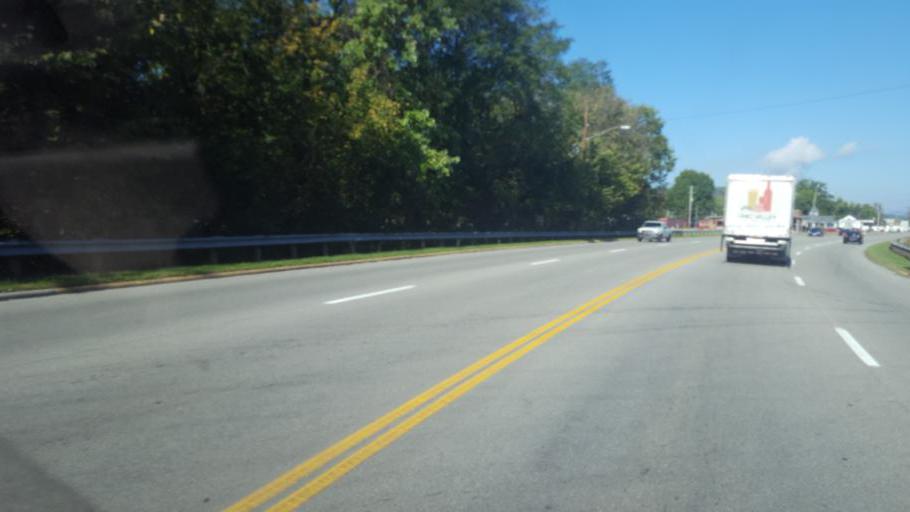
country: US
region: Ohio
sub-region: Brown County
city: Aberdeen
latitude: 38.6567
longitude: -83.7641
